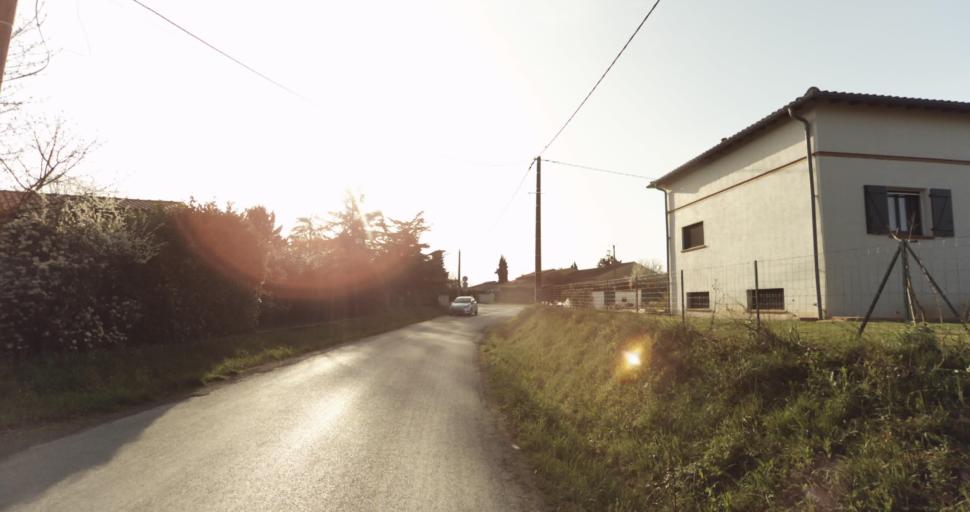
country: FR
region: Midi-Pyrenees
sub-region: Departement du Tarn
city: Saint-Sulpice-la-Pointe
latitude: 43.7667
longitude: 1.6716
